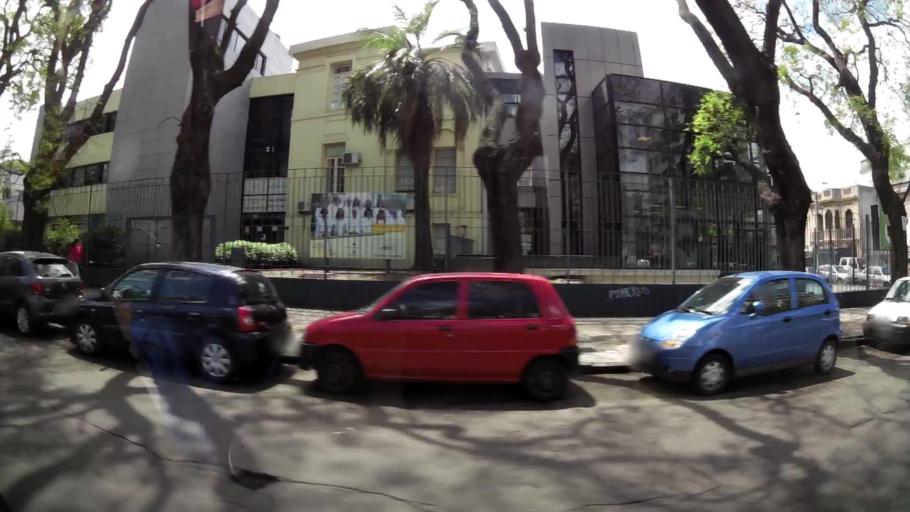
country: UY
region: Montevideo
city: Montevideo
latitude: -34.8996
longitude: -56.1643
